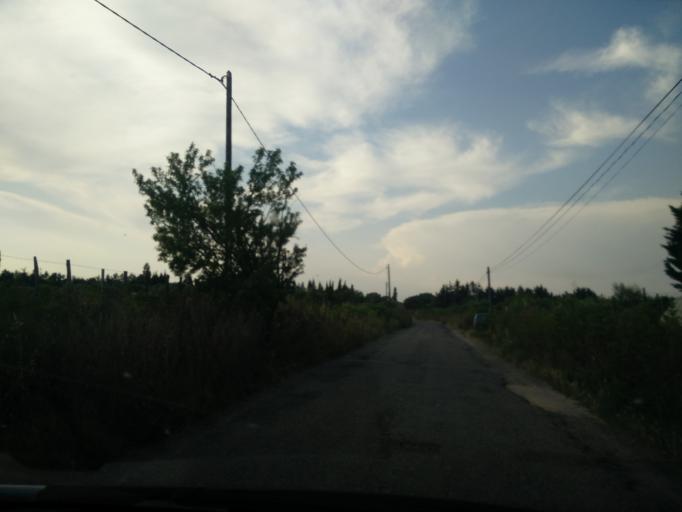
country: FR
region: Languedoc-Roussillon
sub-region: Departement de l'Herault
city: Marsillargues
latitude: 43.6735
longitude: 4.1742
